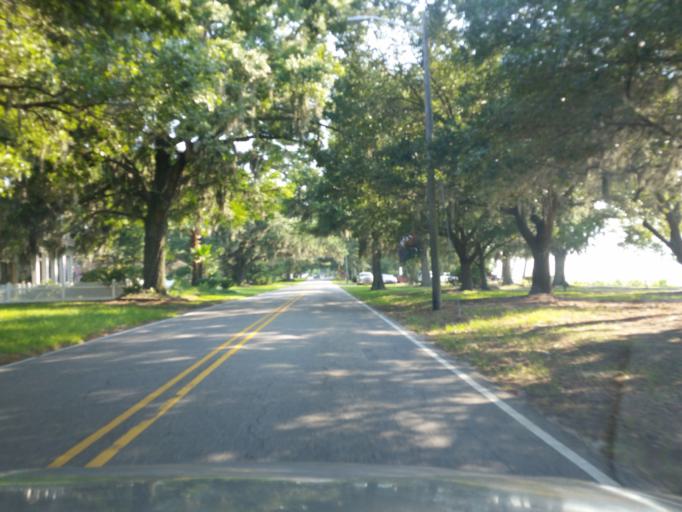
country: US
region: Alabama
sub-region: Baldwin County
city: Fairhope
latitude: 30.5163
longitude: -87.9161
